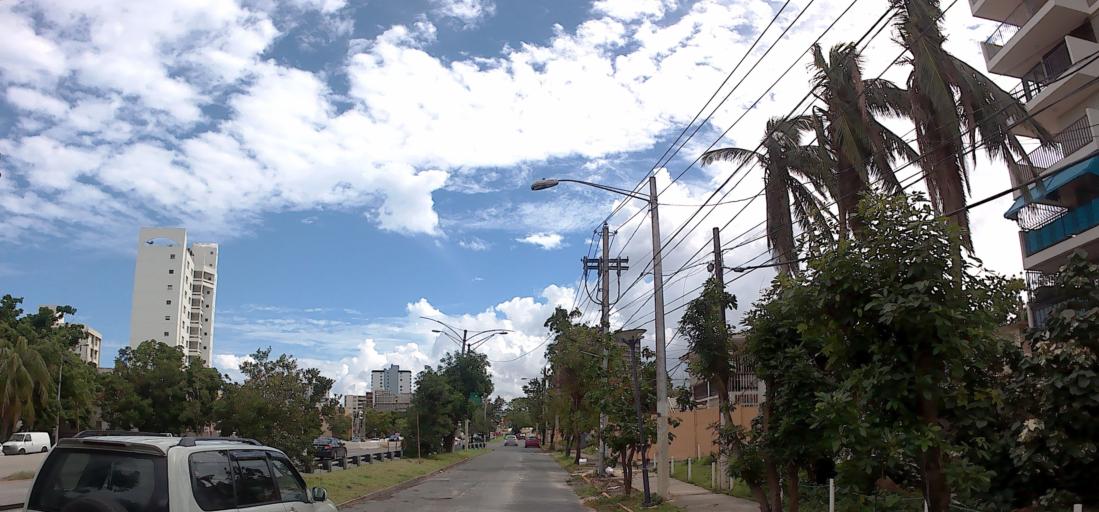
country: PR
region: San Juan
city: San Juan
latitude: 18.4523
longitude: -66.0715
